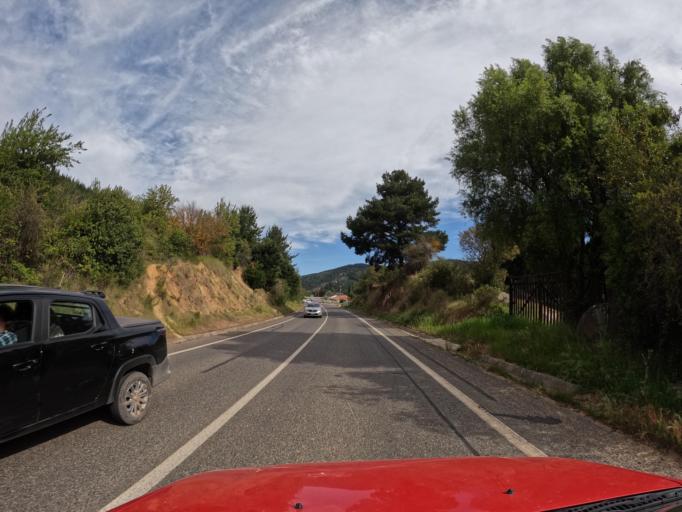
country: CL
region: Maule
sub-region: Provincia de Talca
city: Talca
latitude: -35.3077
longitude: -71.9644
